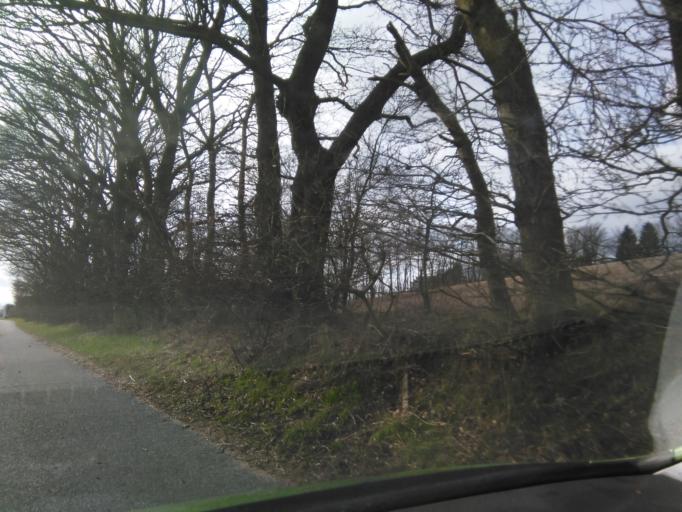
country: DK
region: Central Jutland
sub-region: Arhus Kommune
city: Trige
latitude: 56.2067
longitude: 10.1452
